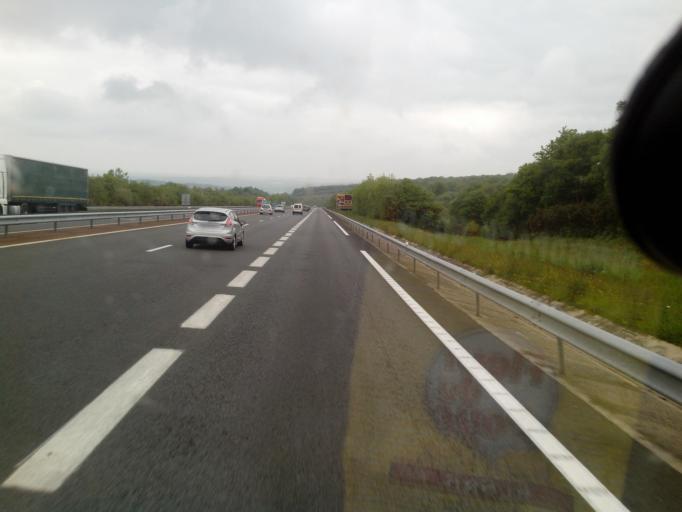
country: FR
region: Lower Normandy
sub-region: Departement de la Manche
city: Tessy-sur-Vire
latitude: 48.9176
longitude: -1.0885
